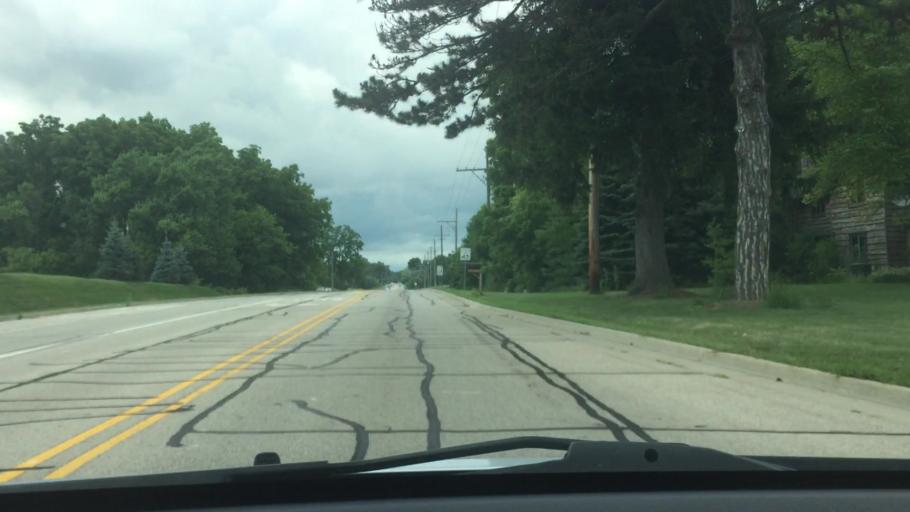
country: US
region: Illinois
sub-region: McHenry County
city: Crystal Lake
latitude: 42.2764
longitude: -88.3208
